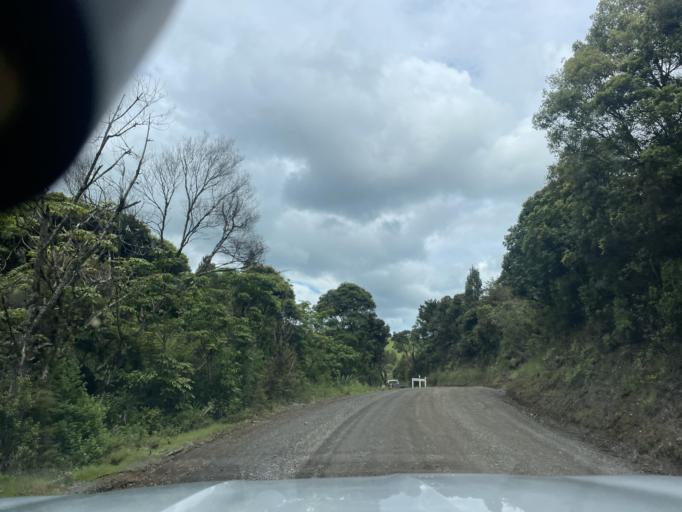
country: NZ
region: Northland
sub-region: Kaipara District
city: Dargaville
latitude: -35.7164
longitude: 173.6400
